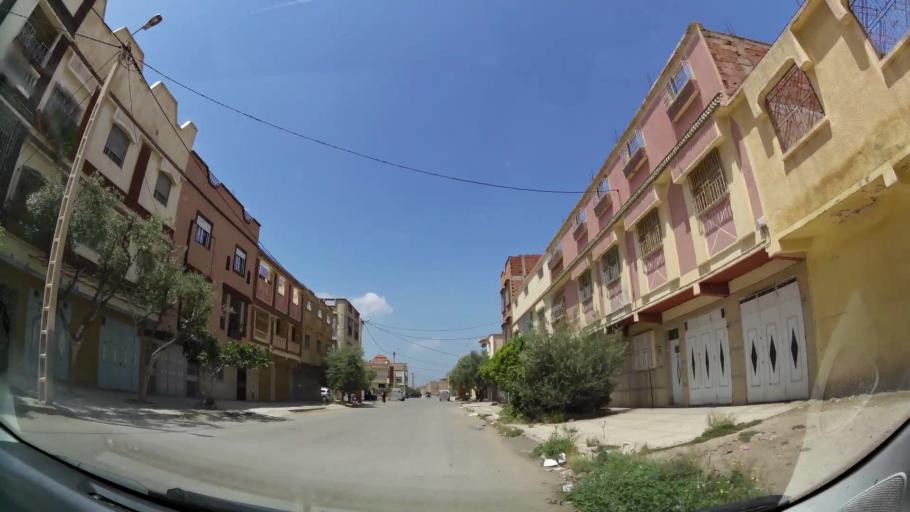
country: MA
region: Oriental
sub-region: Oujda-Angad
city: Oujda
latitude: 34.6864
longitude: -1.8898
